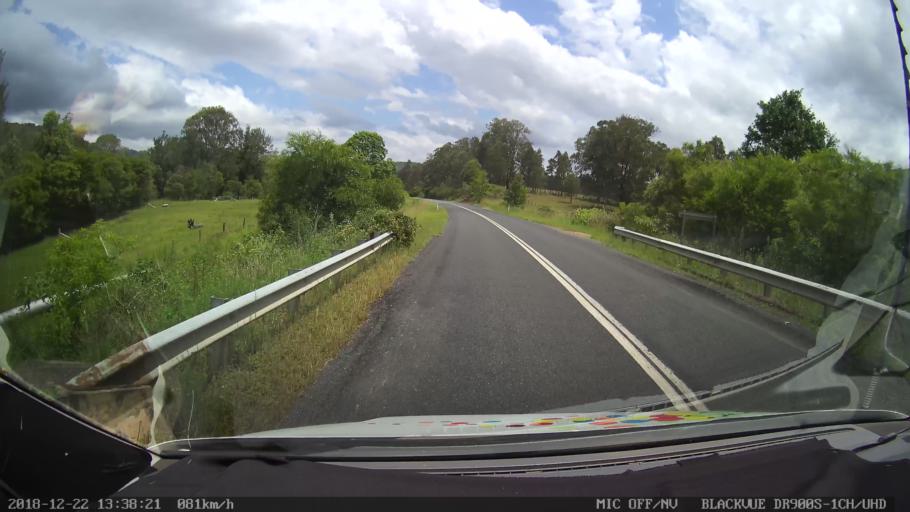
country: AU
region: New South Wales
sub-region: Clarence Valley
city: Coutts Crossing
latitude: -29.8990
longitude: 152.7868
